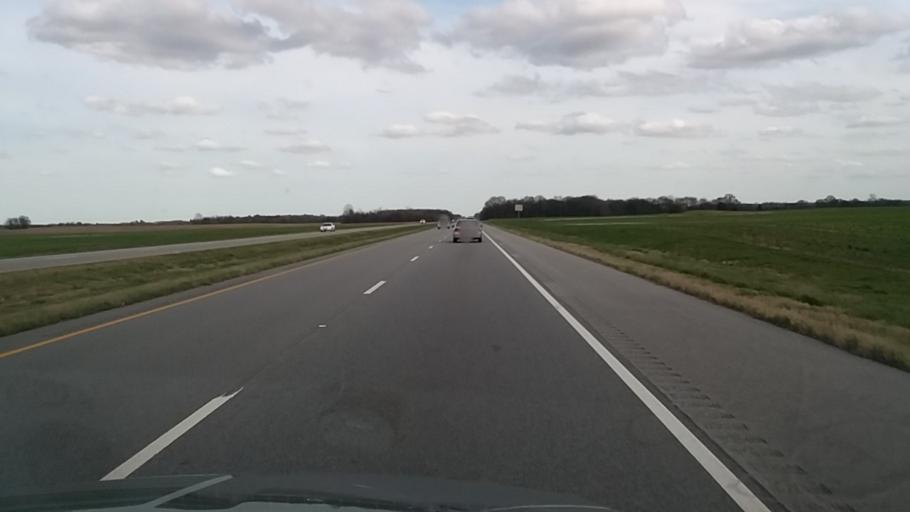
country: US
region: Alabama
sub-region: Lawrence County
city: Town Creek
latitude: 34.6832
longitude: -87.5025
